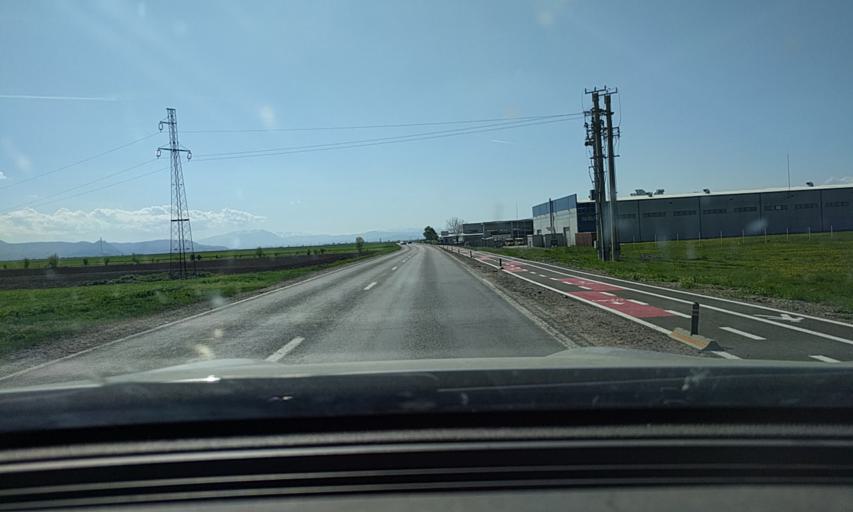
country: RO
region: Brasov
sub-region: Comuna Prejmer
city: Prejmer
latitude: 45.7158
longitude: 25.7474
